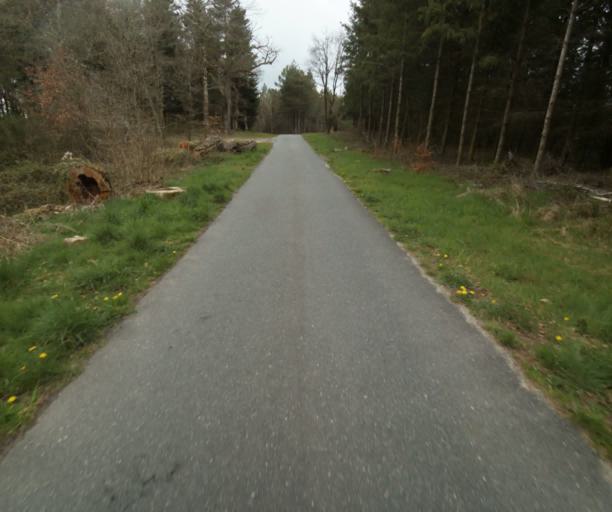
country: FR
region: Limousin
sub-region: Departement de la Correze
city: Correze
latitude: 45.3059
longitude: 1.9066
